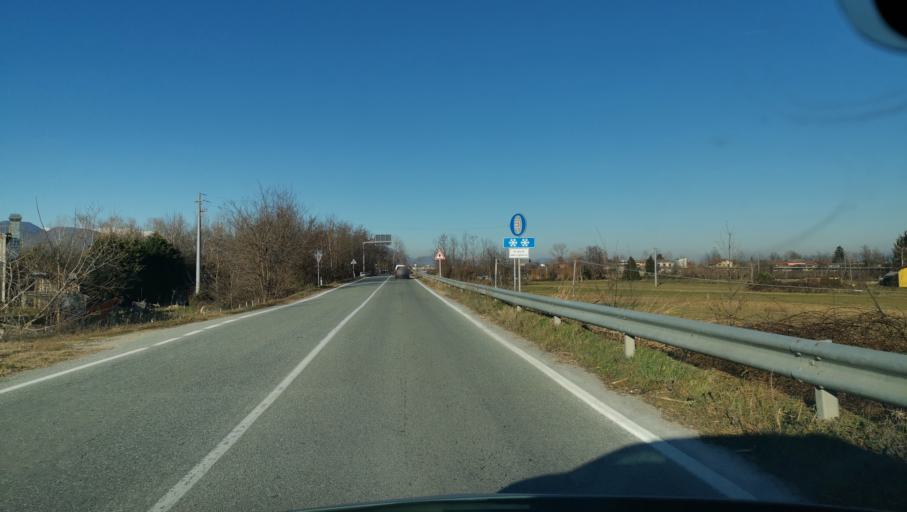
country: IT
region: Piedmont
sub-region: Provincia di Torino
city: Bibiana
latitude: 44.7897
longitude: 7.2936
